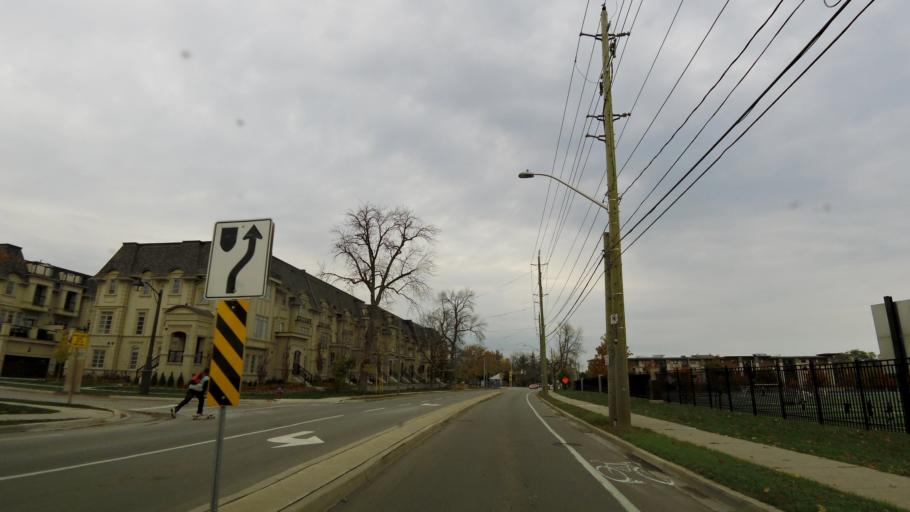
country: CA
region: Ontario
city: Oakville
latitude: 43.4355
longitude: -79.6830
